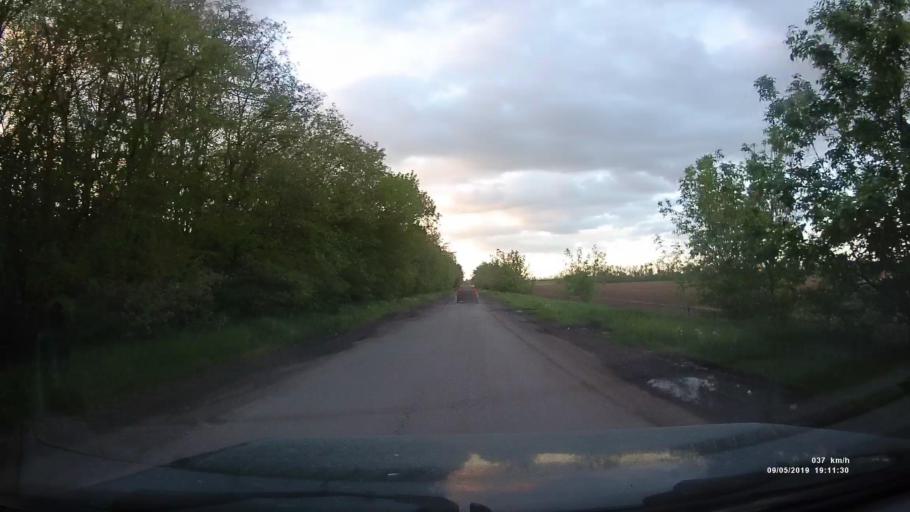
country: RU
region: Krasnodarskiy
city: Kanelovskaya
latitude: 46.7357
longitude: 39.2136
